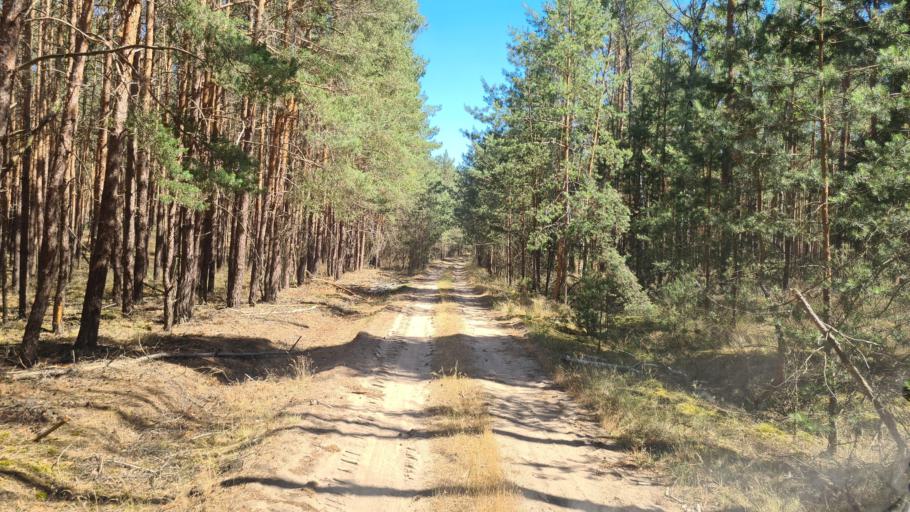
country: DE
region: Brandenburg
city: Treuenbrietzen
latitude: 52.0559
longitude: 12.7973
